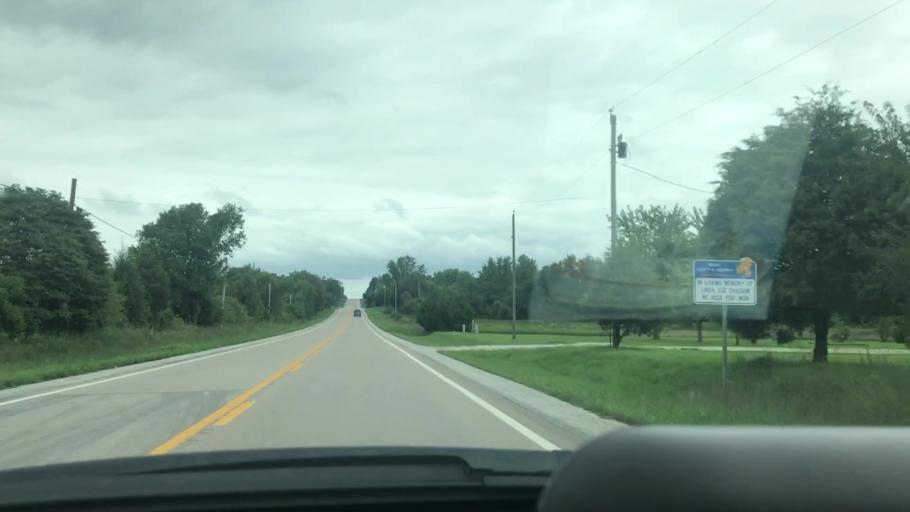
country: US
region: Missouri
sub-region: Dallas County
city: Buffalo
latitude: 37.6965
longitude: -93.1038
